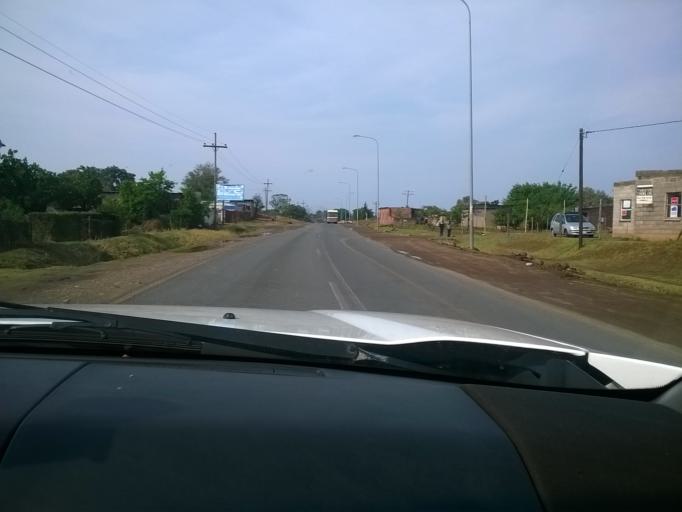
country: LS
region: Berea
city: Teyateyaneng
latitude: -29.1439
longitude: 27.7496
